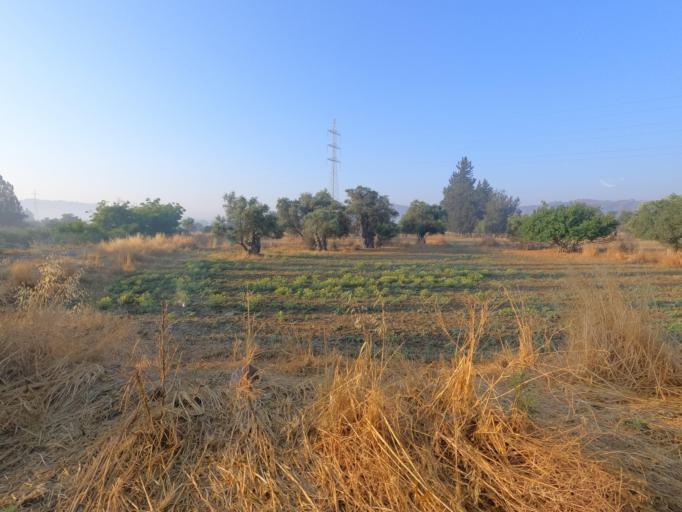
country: CY
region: Larnaka
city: Mosfiloti
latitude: 34.9737
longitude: 33.4400
